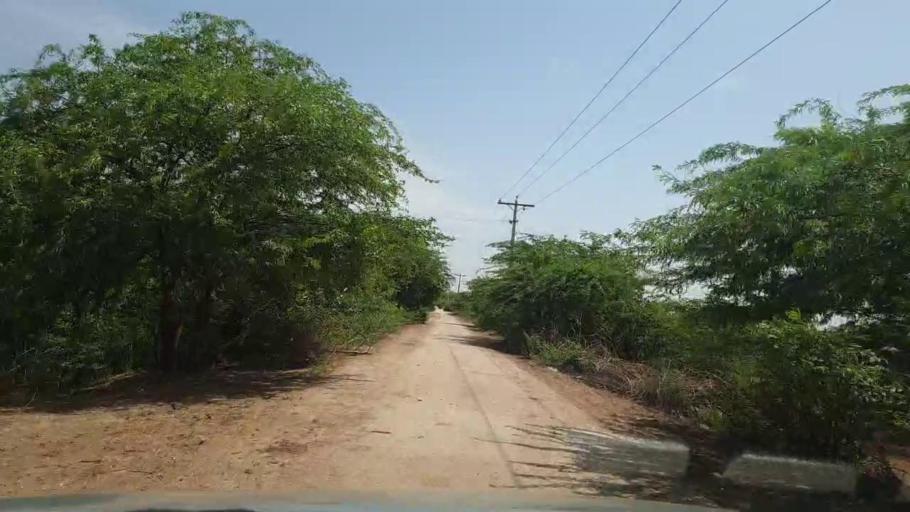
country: PK
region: Sindh
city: Bozdar
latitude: 27.1090
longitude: 68.9834
